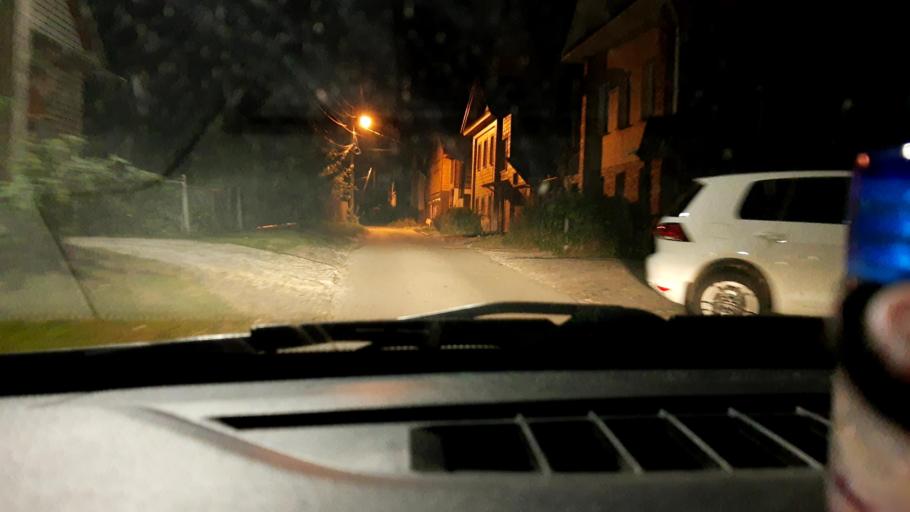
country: RU
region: Nizjnij Novgorod
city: Kstovo
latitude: 56.1560
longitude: 44.2414
